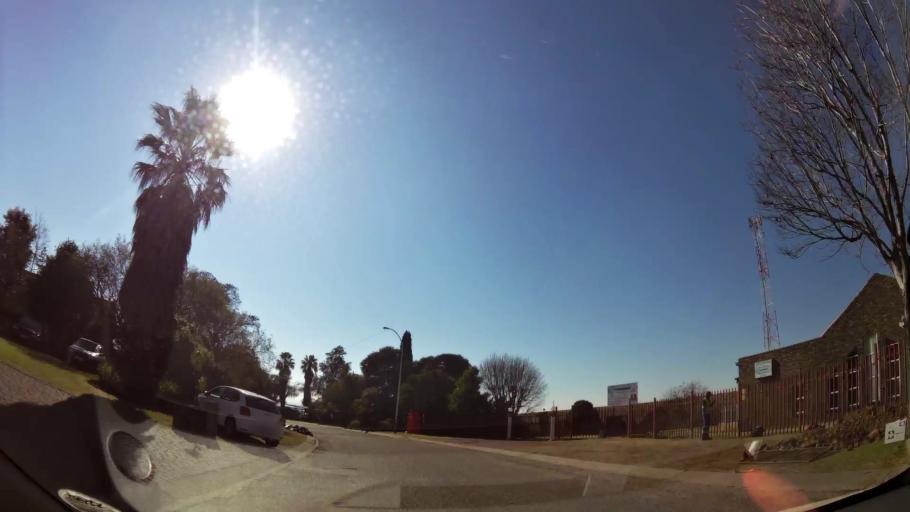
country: ZA
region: Mpumalanga
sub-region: Nkangala District Municipality
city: Witbank
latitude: -25.8756
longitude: 29.2527
